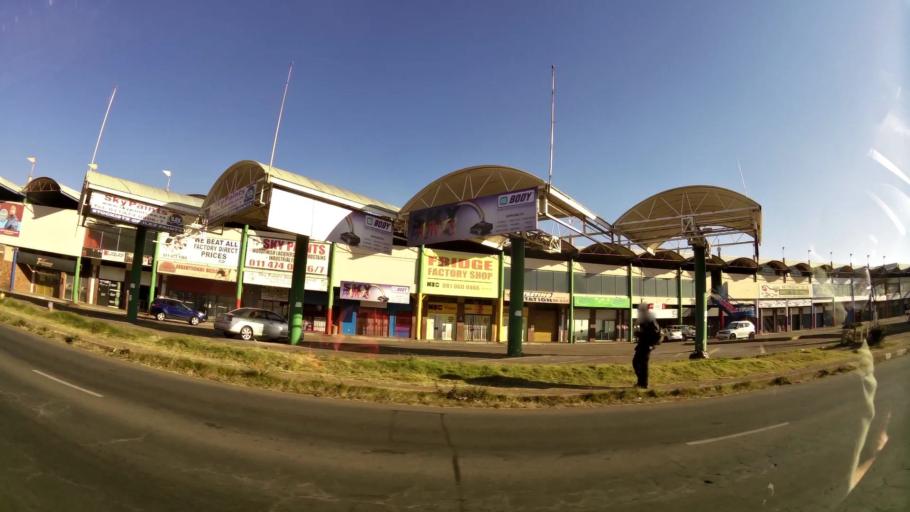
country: ZA
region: Gauteng
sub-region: City of Johannesburg Metropolitan Municipality
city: Johannesburg
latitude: -26.2030
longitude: 27.9721
